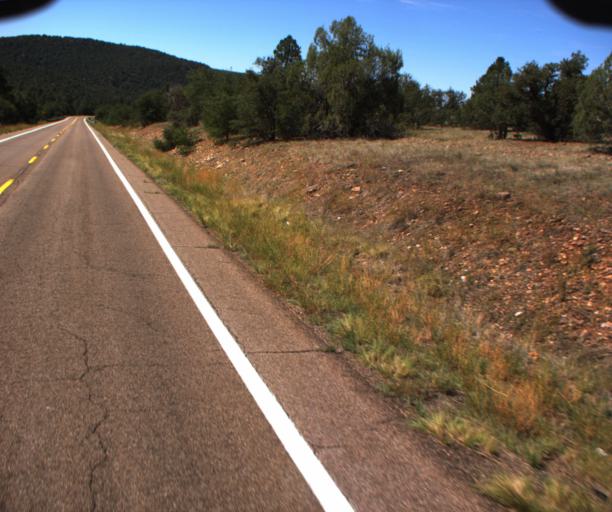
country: US
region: Arizona
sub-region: Navajo County
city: Cibecue
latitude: 33.9090
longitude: -110.3632
